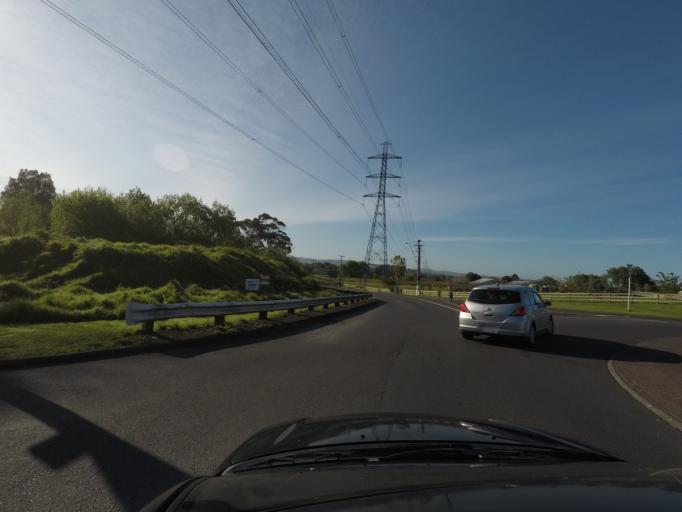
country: NZ
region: Auckland
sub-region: Auckland
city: Takanini
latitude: -37.0156
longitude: 174.9211
